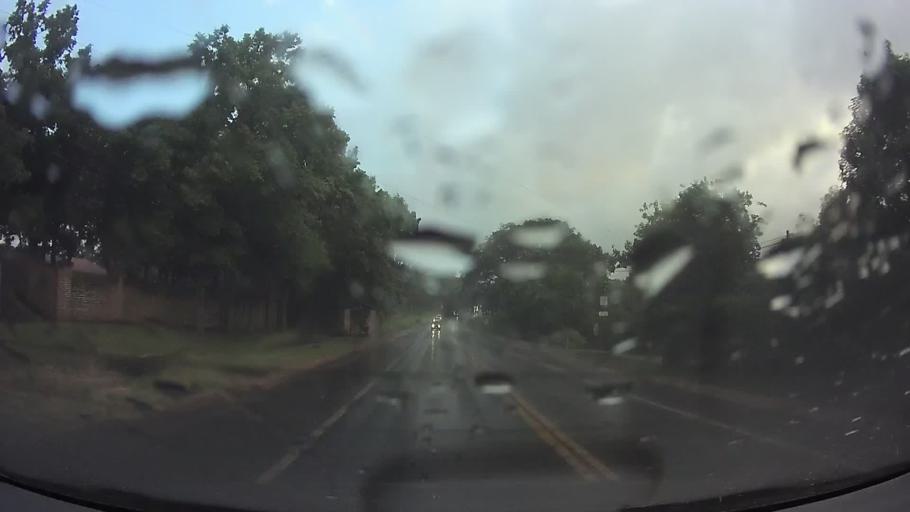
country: PY
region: Paraguari
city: Yaguaron
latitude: -25.5858
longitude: -57.2396
